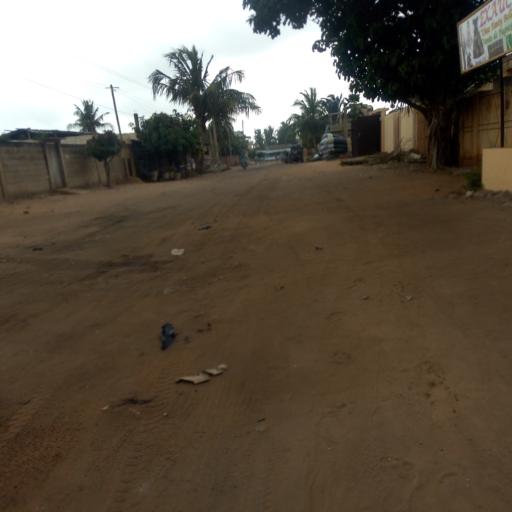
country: TG
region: Maritime
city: Lome
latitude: 6.1916
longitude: 1.2593
